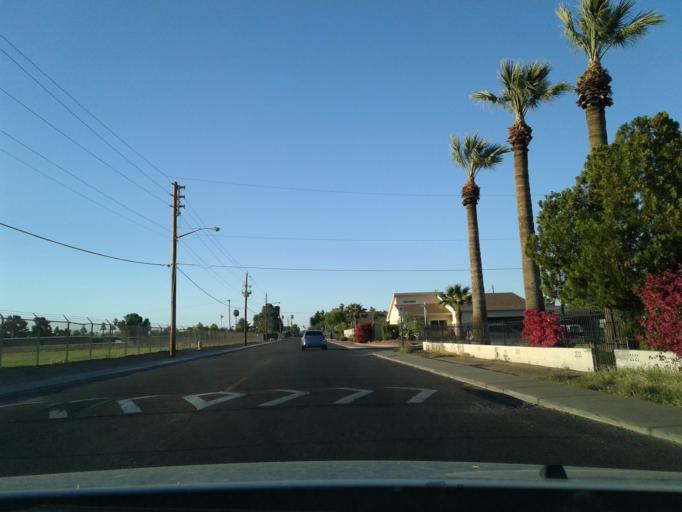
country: US
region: Arizona
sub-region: Maricopa County
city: Glendale
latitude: 33.5349
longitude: -112.1039
